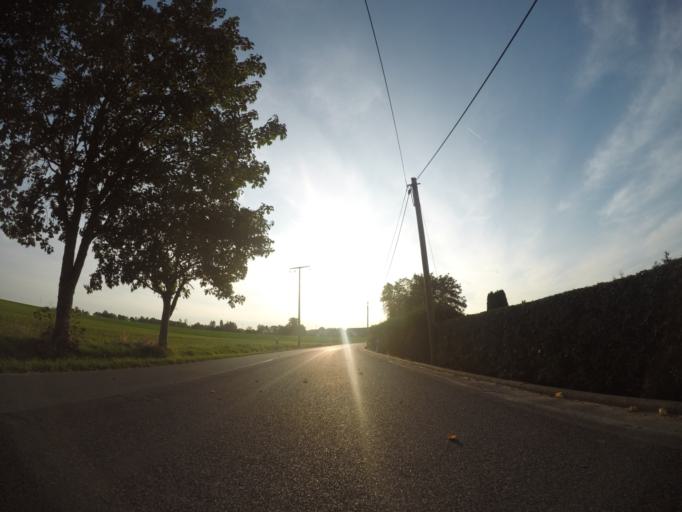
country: DE
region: Thuringia
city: Altkirchen
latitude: 50.9345
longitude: 12.3667
